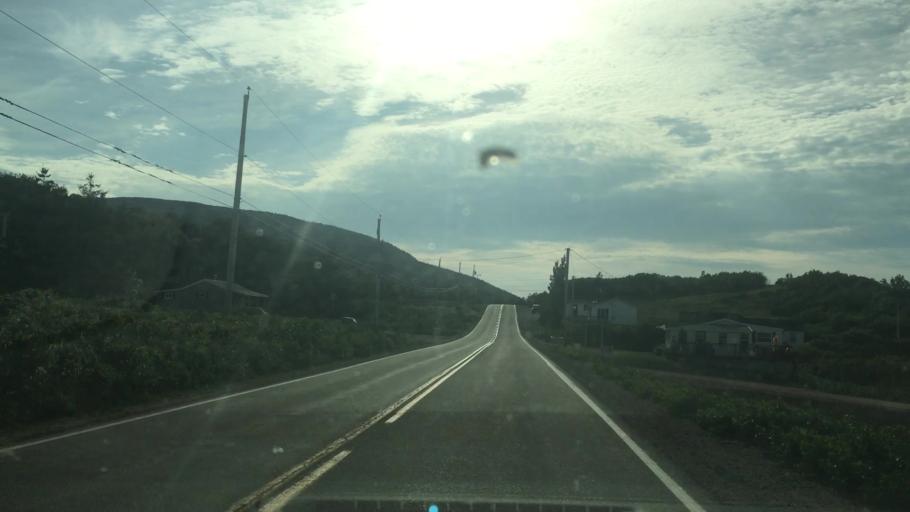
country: CA
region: Nova Scotia
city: Sydney Mines
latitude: 46.8246
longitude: -60.8165
